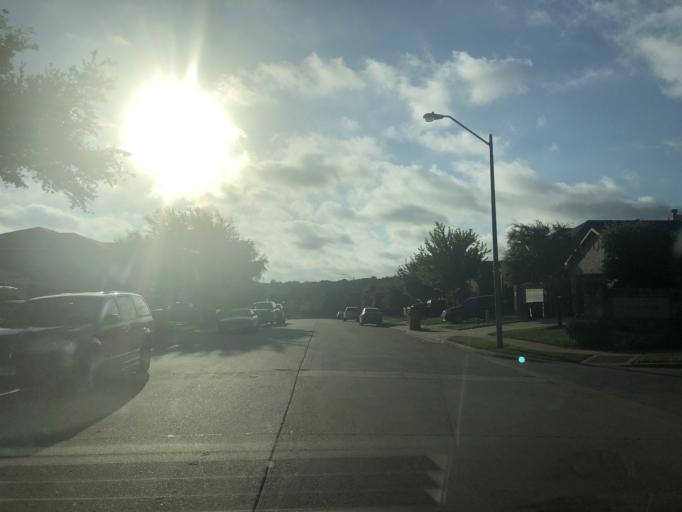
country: US
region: Texas
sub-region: Dallas County
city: Duncanville
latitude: 32.6673
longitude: -96.9412
